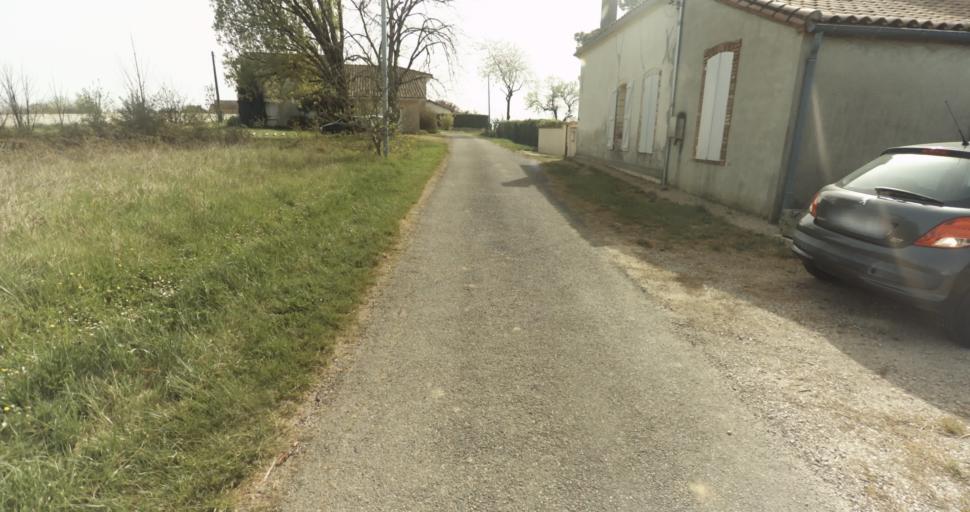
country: FR
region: Midi-Pyrenees
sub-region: Departement du Tarn-et-Garonne
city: Moissac
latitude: 44.1314
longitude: 1.0638
